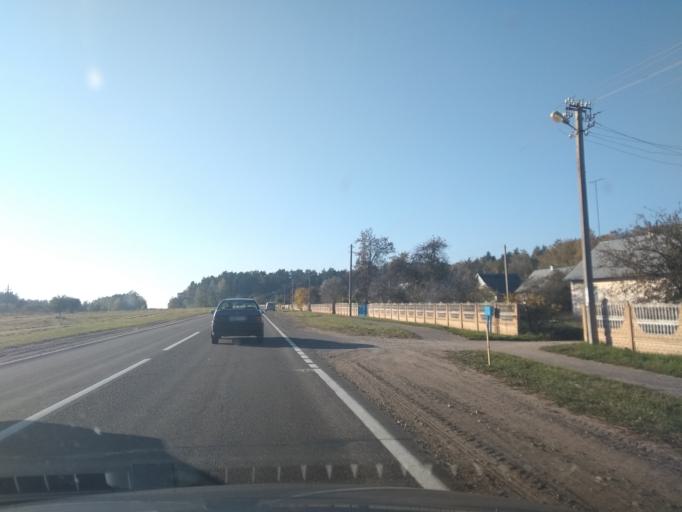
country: BY
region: Grodnenskaya
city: Vyalikaya Byerastavitsa
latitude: 53.1175
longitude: 23.9630
